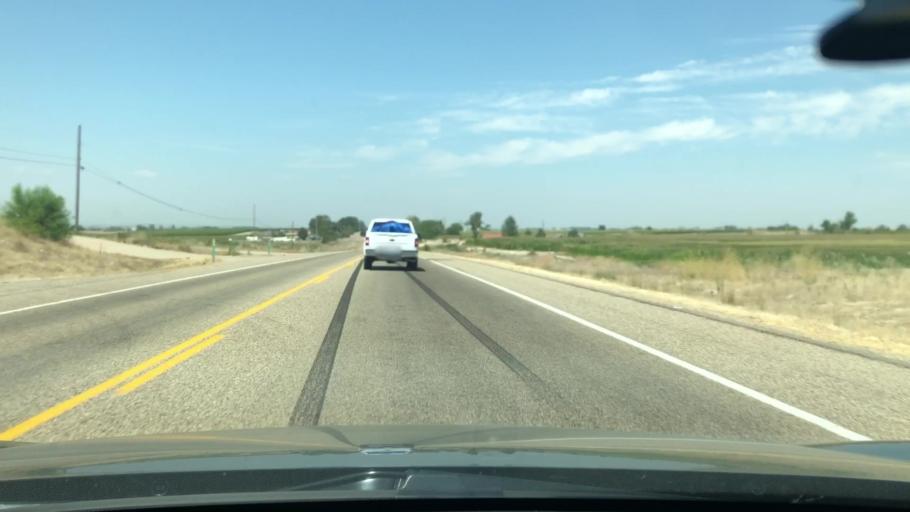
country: US
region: Idaho
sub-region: Canyon County
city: Parma
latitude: 43.8274
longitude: -116.9545
